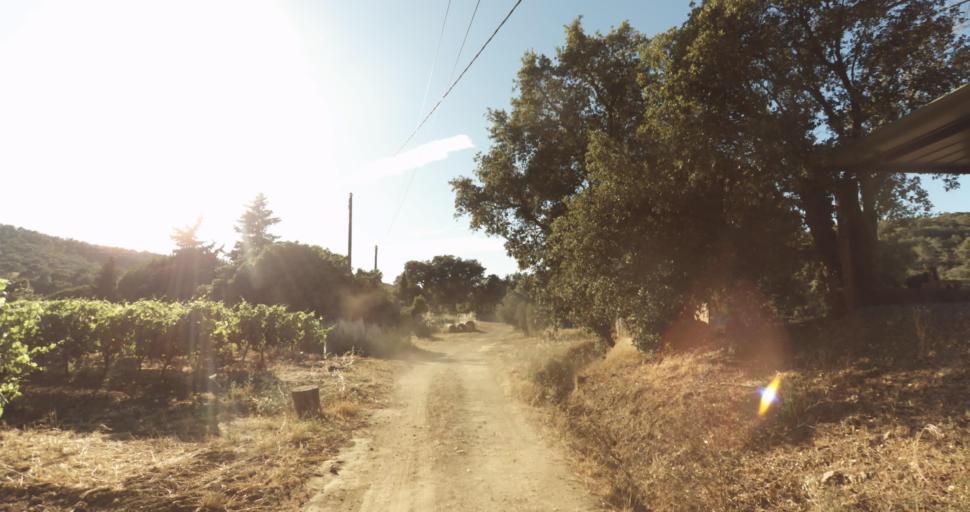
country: FR
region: Provence-Alpes-Cote d'Azur
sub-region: Departement du Var
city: La Croix-Valmer
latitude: 43.2207
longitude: 6.5617
